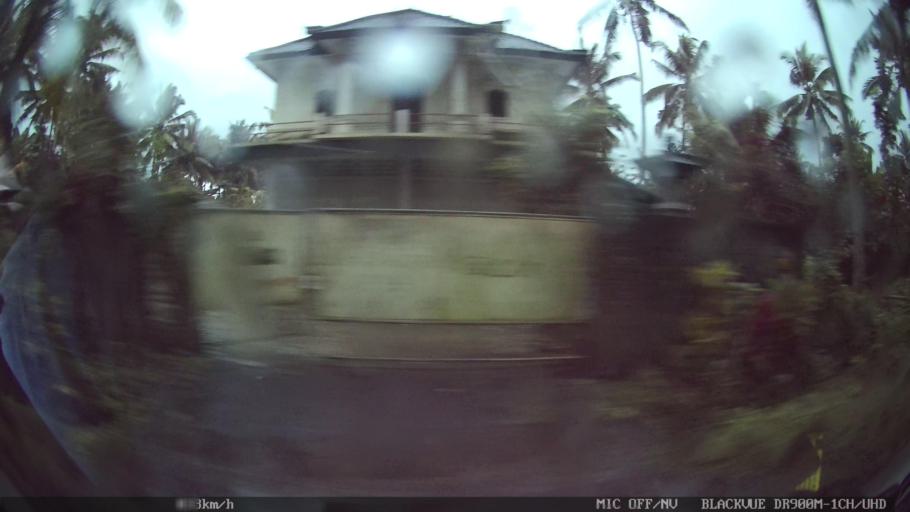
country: ID
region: Bali
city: Kekeran
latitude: -8.4795
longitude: 115.1846
